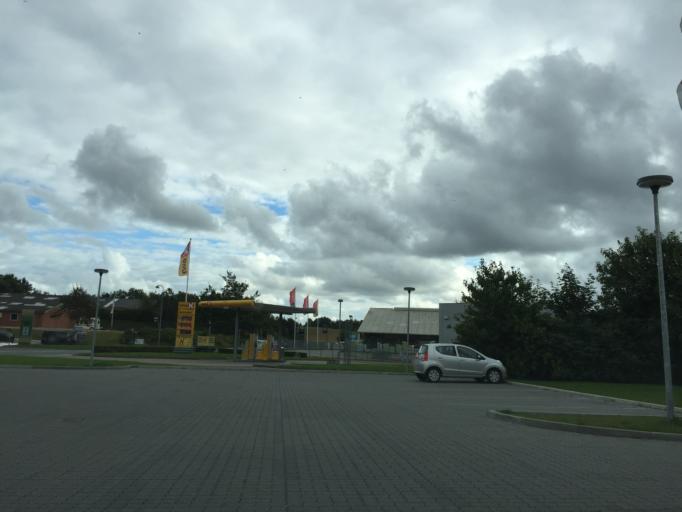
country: DK
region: Central Jutland
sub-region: Favrskov Kommune
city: Hammel
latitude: 56.2213
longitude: 9.7427
